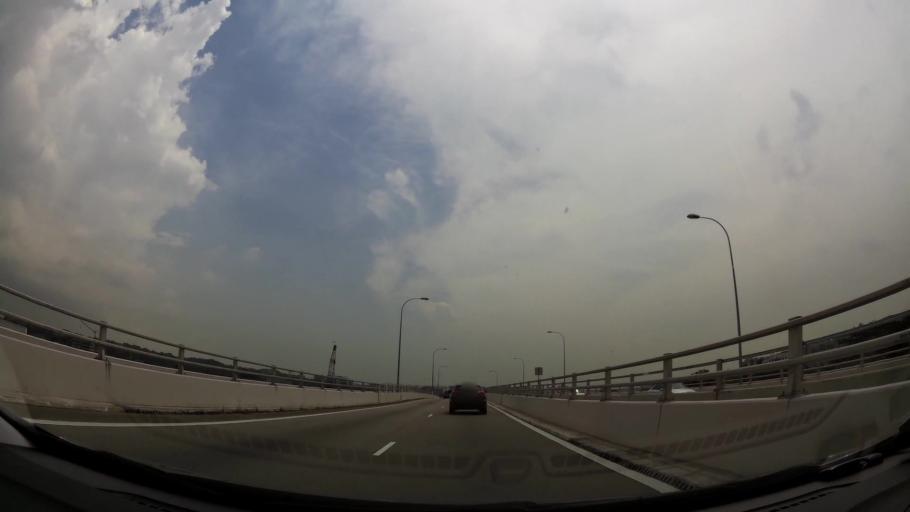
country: SG
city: Singapore
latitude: 1.3429
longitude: 103.8936
